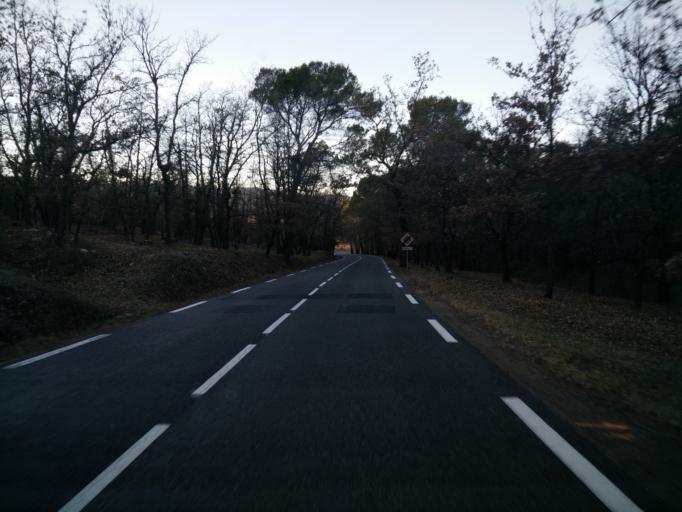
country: FR
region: Provence-Alpes-Cote d'Azur
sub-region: Departement du Var
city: Figanieres
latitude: 43.5511
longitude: 6.5259
